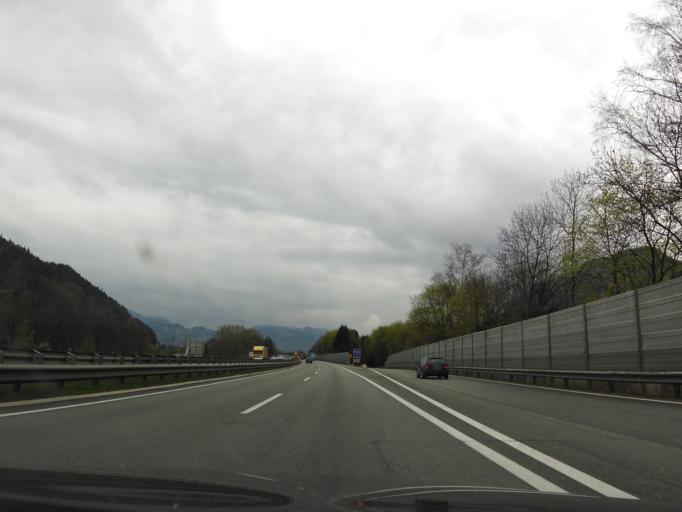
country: AT
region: Tyrol
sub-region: Politischer Bezirk Kufstein
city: Kufstein
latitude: 47.5941
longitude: 12.1728
